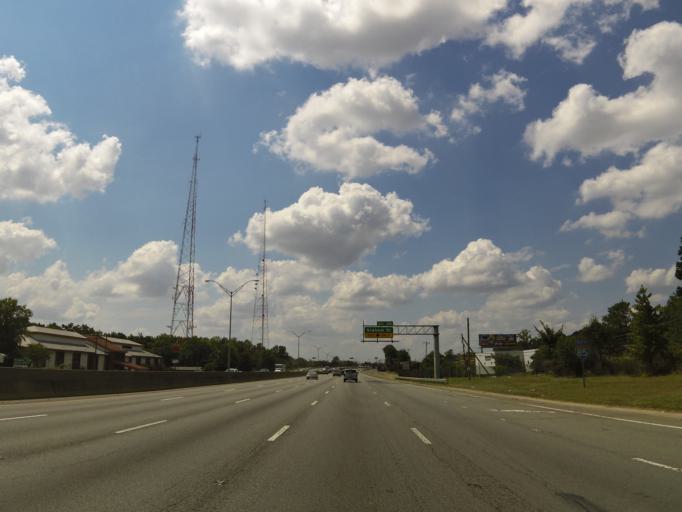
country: US
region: North Carolina
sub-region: Mecklenburg County
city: Charlotte
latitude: 35.2783
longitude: -80.7965
